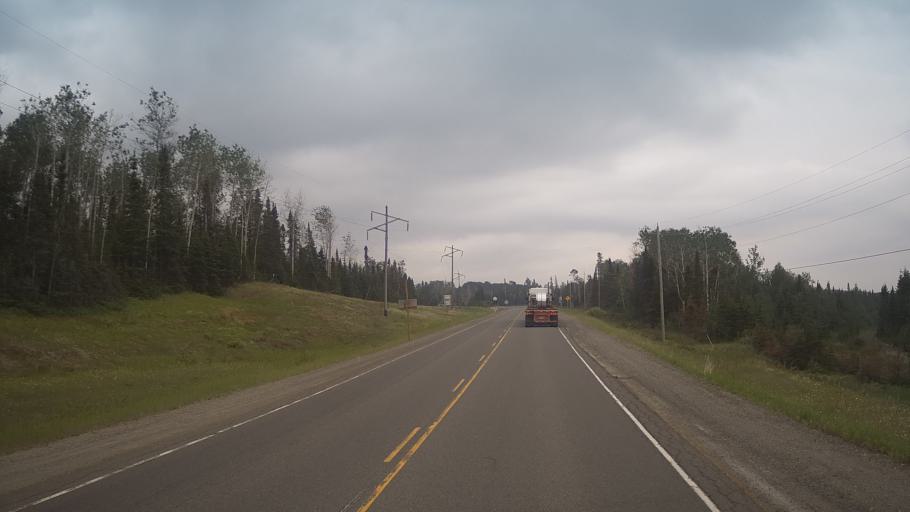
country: CA
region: Ontario
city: Greenstone
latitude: 49.5821
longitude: -87.9716
